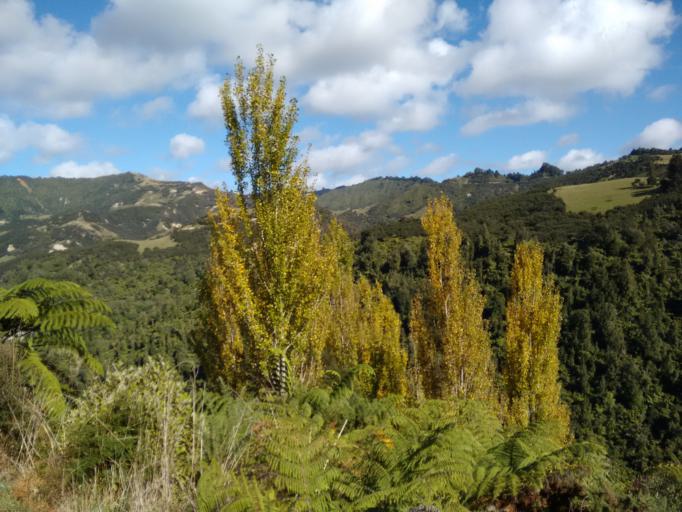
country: NZ
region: Manawatu-Wanganui
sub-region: Wanganui District
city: Wanganui
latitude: -39.5332
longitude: 175.0644
